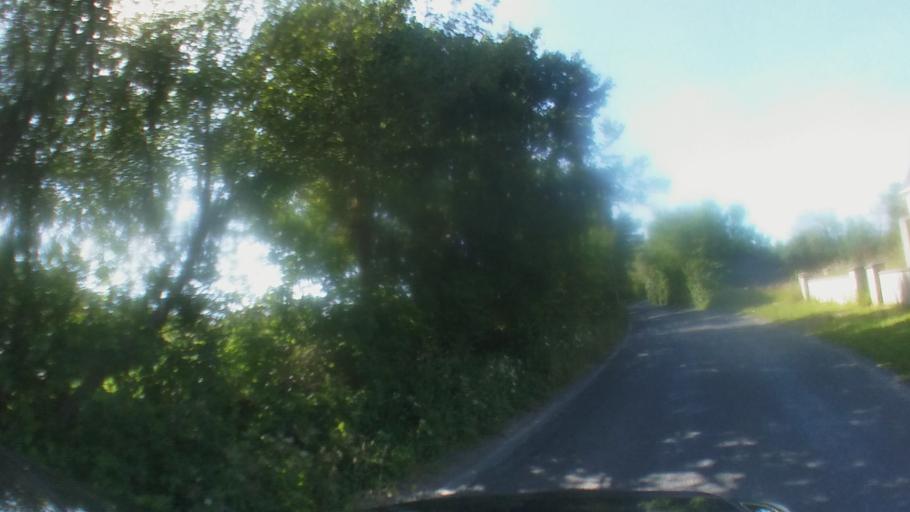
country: IE
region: Leinster
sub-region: Loch Garman
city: Loch Garman
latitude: 52.2234
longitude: -6.5436
